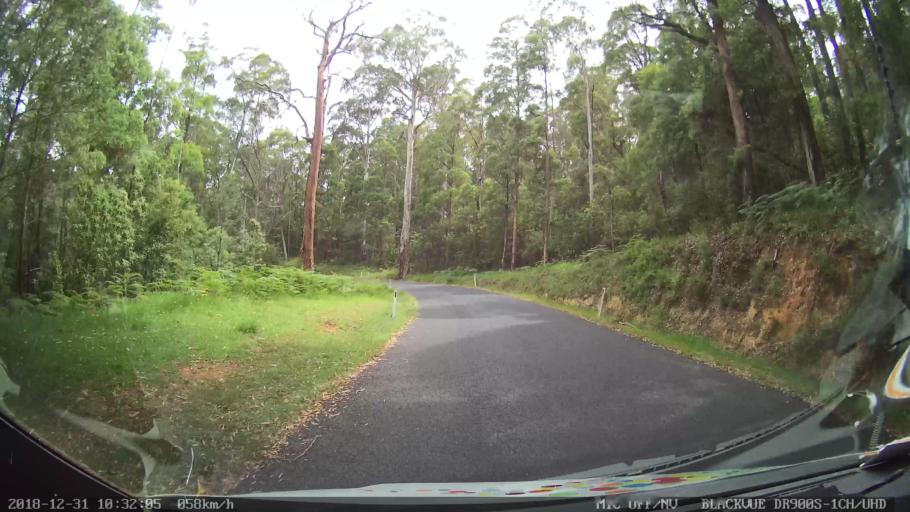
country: AU
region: New South Wales
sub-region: Snowy River
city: Jindabyne
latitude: -36.4533
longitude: 148.1602
